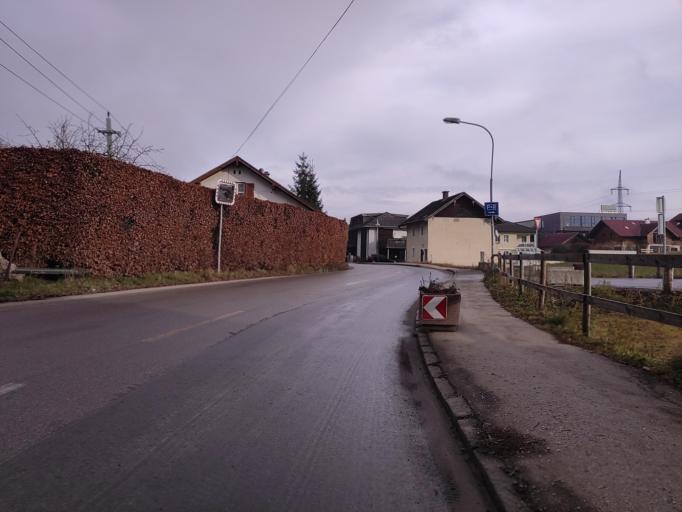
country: AT
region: Salzburg
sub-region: Politischer Bezirk Salzburg-Umgebung
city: Neumarkt am Wallersee
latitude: 47.9530
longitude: 13.2234
